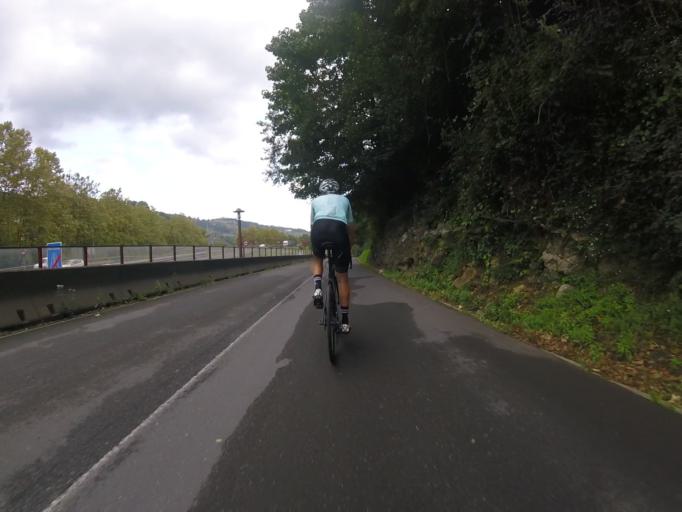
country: ES
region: Basque Country
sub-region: Provincia de Guipuzcoa
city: Tolosa
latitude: 43.1217
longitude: -2.0887
